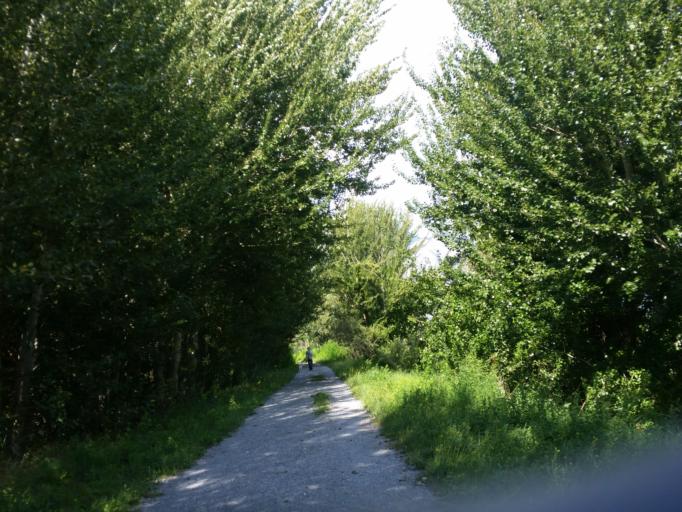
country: CH
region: Valais
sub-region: Martigny District
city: Saillon
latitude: 46.1663
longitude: 7.1996
